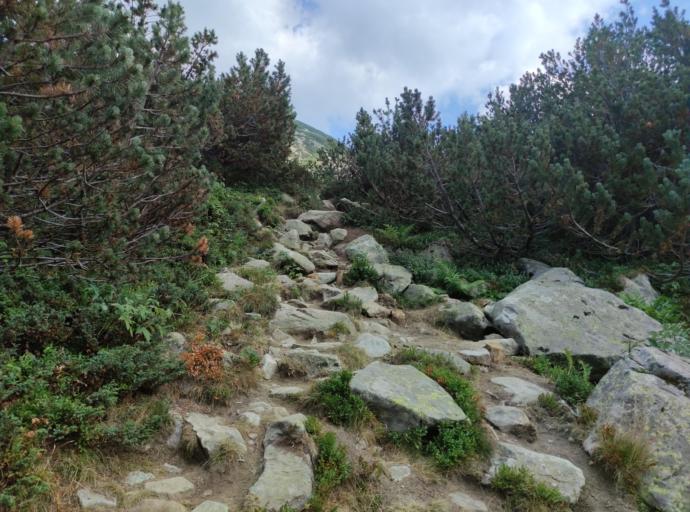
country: BG
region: Blagoevgrad
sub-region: Obshtina Bansko
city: Bansko
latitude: 41.7516
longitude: 23.4145
